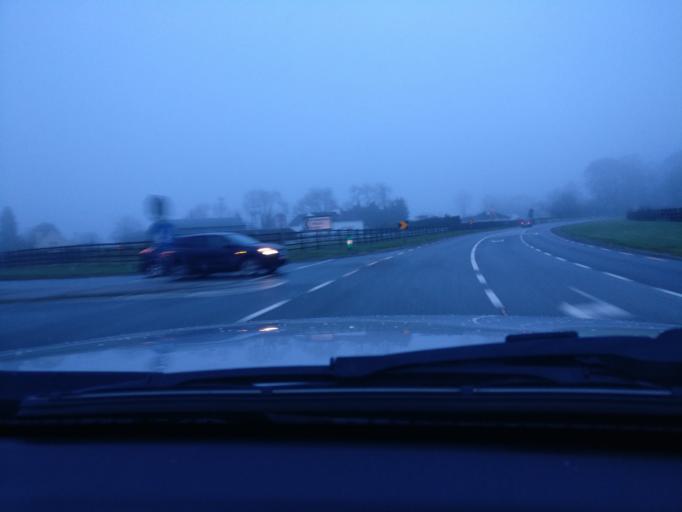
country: IE
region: Leinster
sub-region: An Mhi
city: Athboy
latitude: 53.6378
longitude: -6.8933
